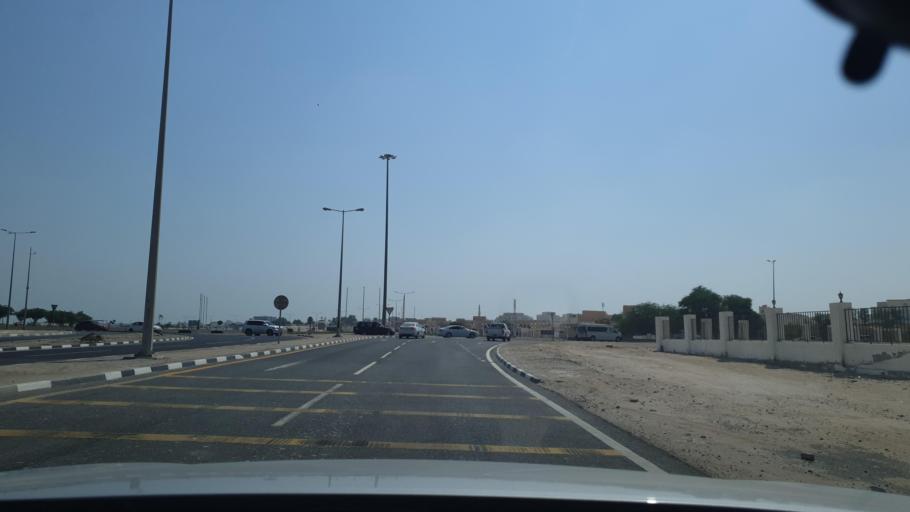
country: QA
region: Al Khawr
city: Al Khawr
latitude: 25.6914
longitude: 51.4991
